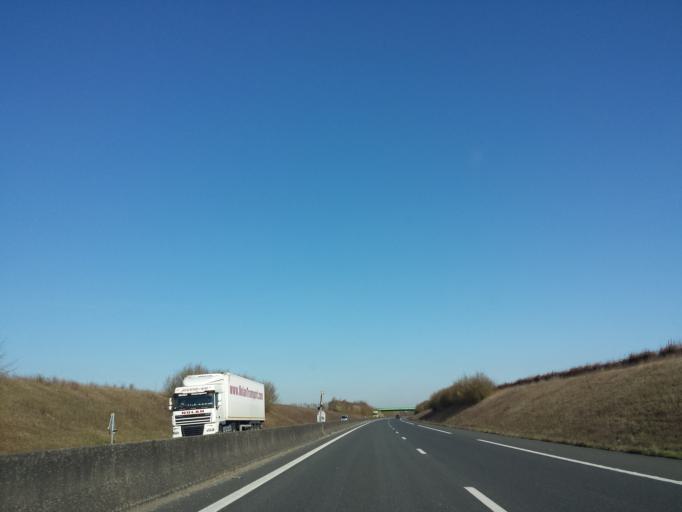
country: FR
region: Picardie
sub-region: Departement de l'Oise
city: Tille
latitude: 49.4886
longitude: 2.1663
